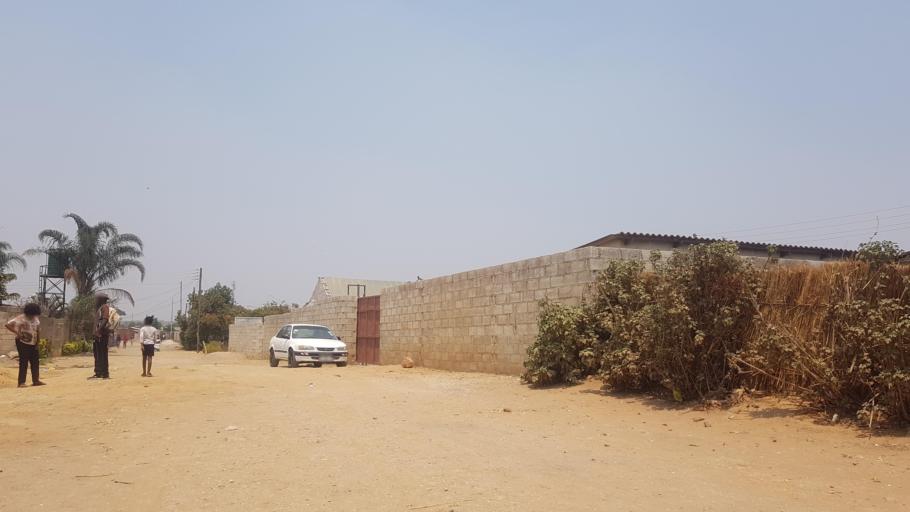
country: ZM
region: Lusaka
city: Lusaka
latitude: -15.4390
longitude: 28.3766
